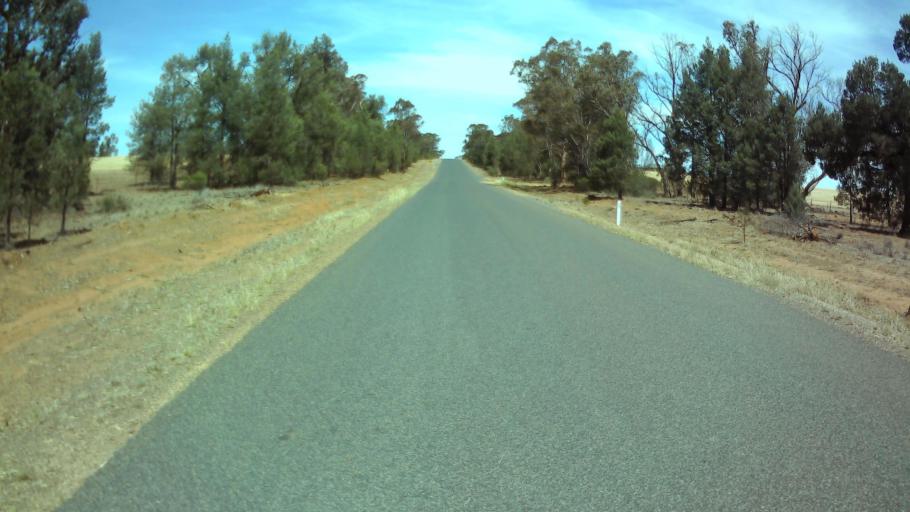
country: AU
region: New South Wales
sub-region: Weddin
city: Grenfell
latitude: -33.8991
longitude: 147.7536
